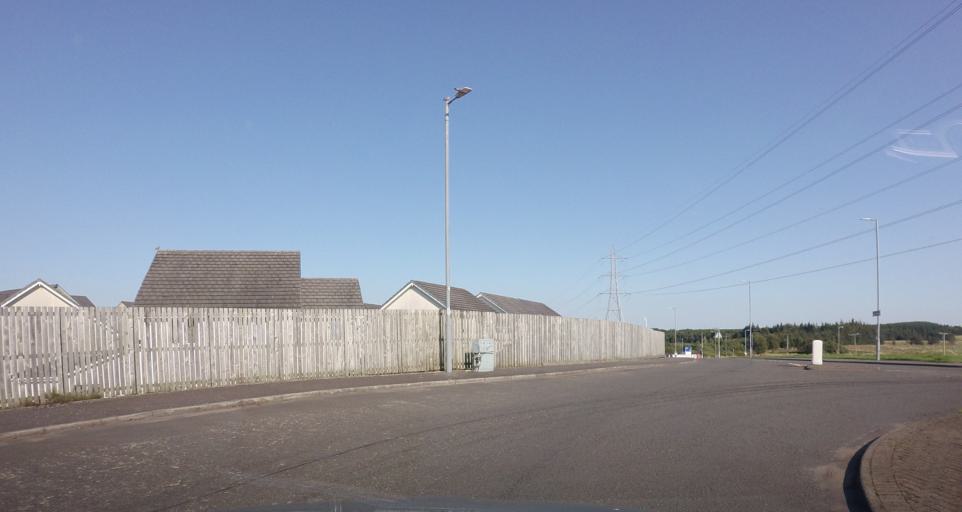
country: GB
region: Scotland
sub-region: South Lanarkshire
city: East Kilbride
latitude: 55.7409
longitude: -4.1945
